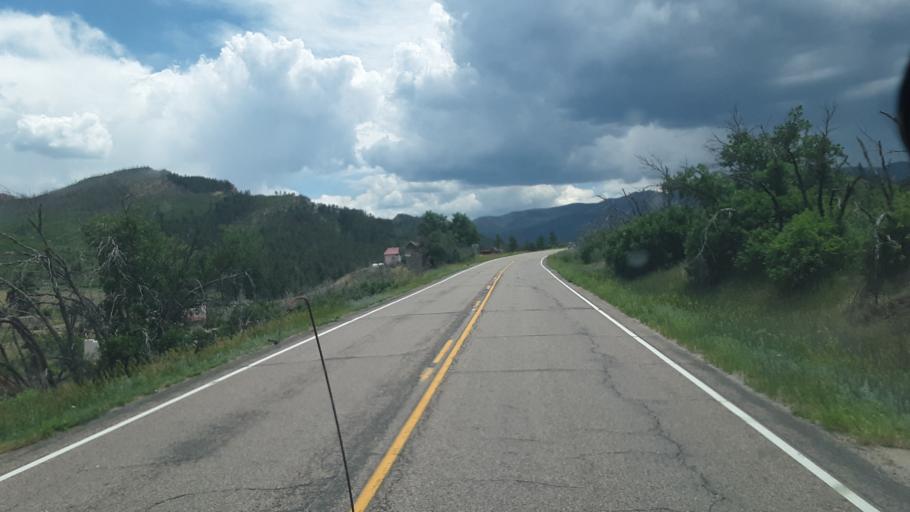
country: US
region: Colorado
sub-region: Fremont County
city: Florence
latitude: 38.2152
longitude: -105.0936
